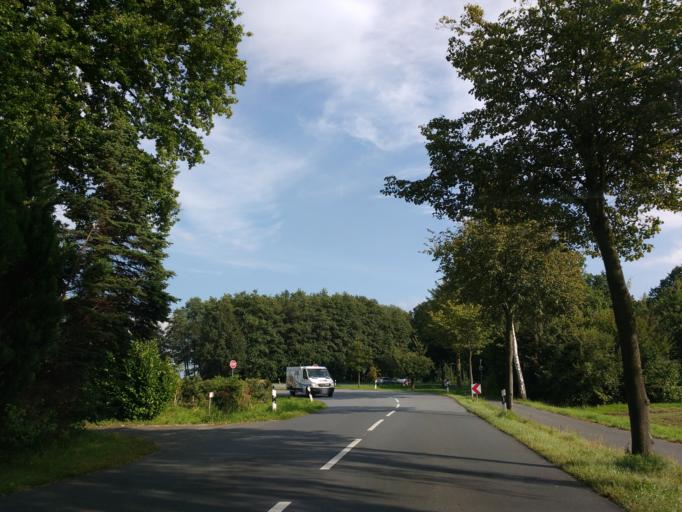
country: DE
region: North Rhine-Westphalia
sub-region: Regierungsbezirk Detmold
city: Delbruck
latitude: 51.7903
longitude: 8.5617
